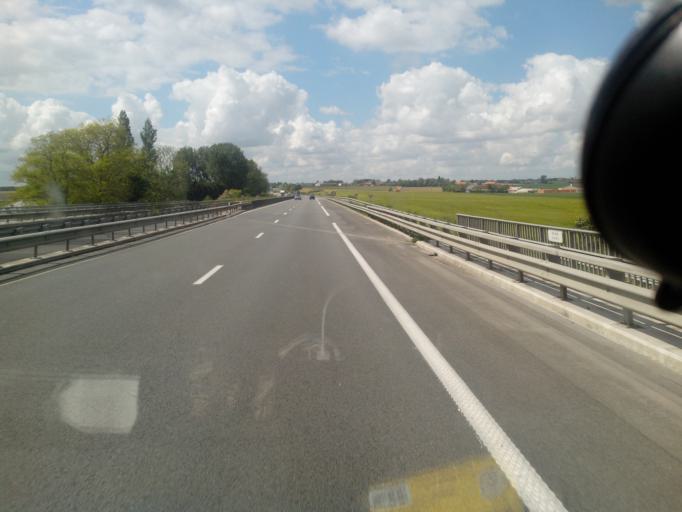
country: FR
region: Nord-Pas-de-Calais
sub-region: Departement du Nord
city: Meteren
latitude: 50.7438
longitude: 2.6773
